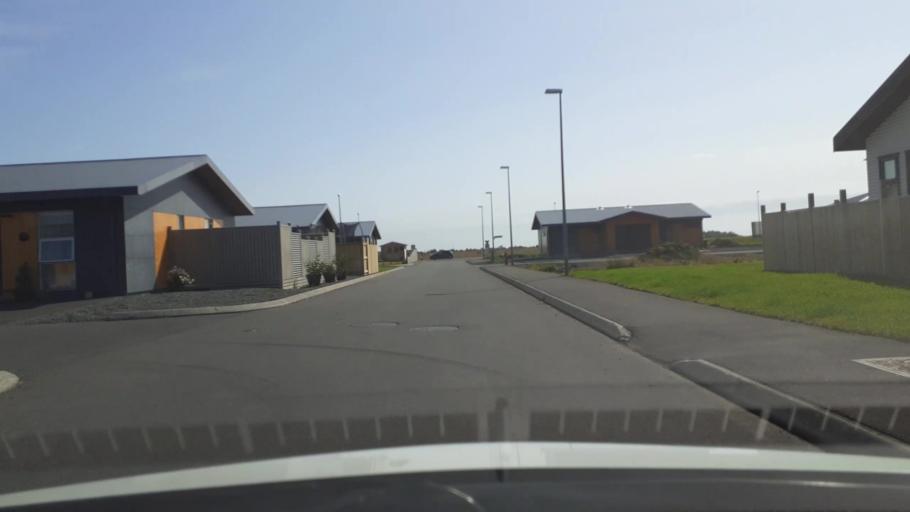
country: IS
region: South
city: Selfoss
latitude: 63.9252
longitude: -20.9841
